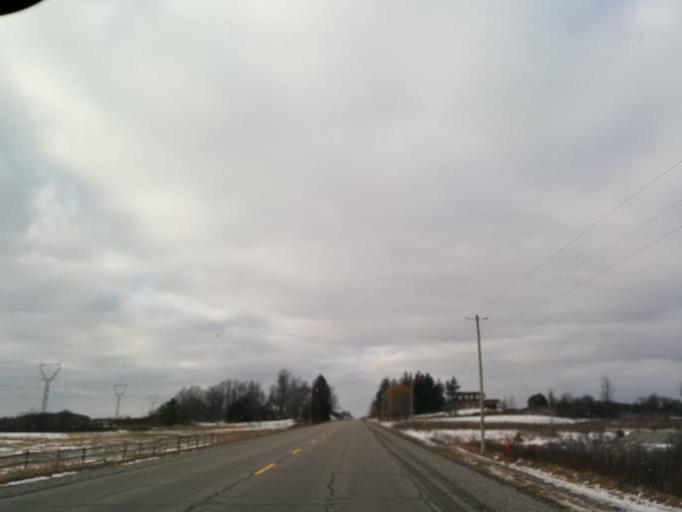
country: CA
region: Ontario
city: Brantford
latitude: 42.9783
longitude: -80.0957
